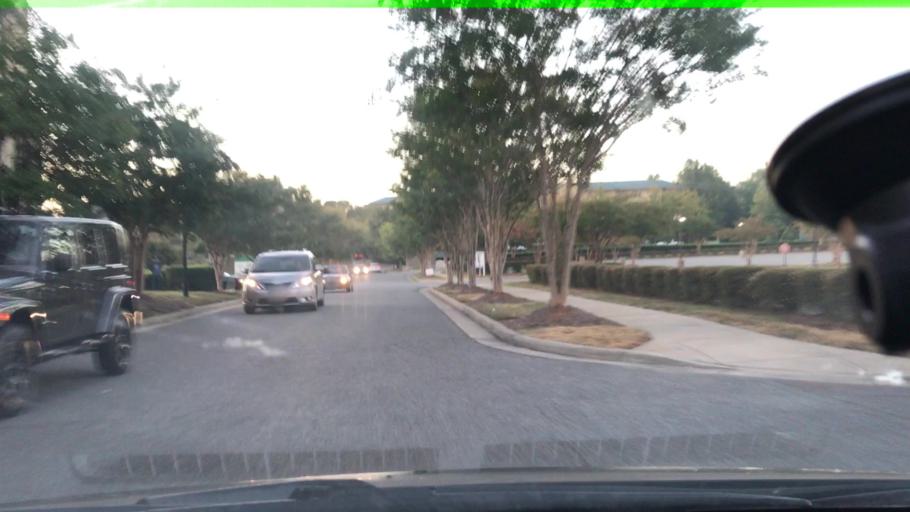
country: US
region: North Carolina
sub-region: Mecklenburg County
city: Cornelius
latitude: 35.4473
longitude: -80.8912
